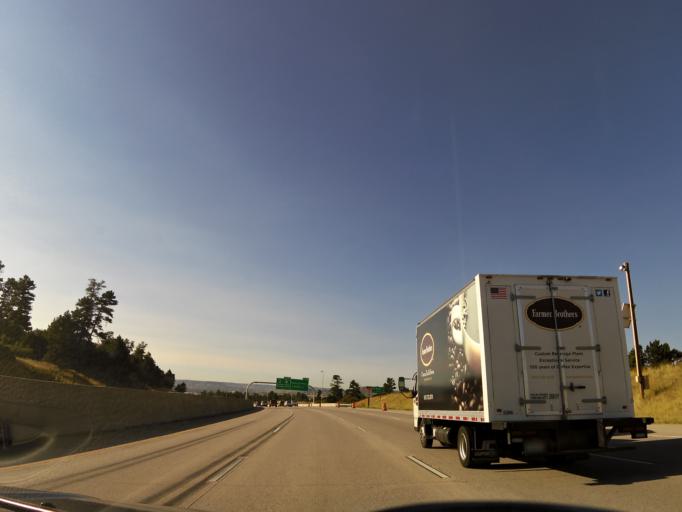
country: US
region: Colorado
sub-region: Douglas County
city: Castle Pines
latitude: 39.4316
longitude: -104.8796
